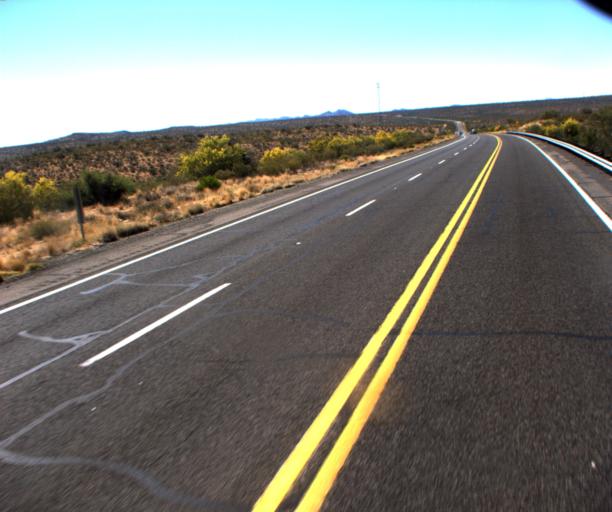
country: US
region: Arizona
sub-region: Yavapai County
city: Congress
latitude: 34.2226
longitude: -113.0692
